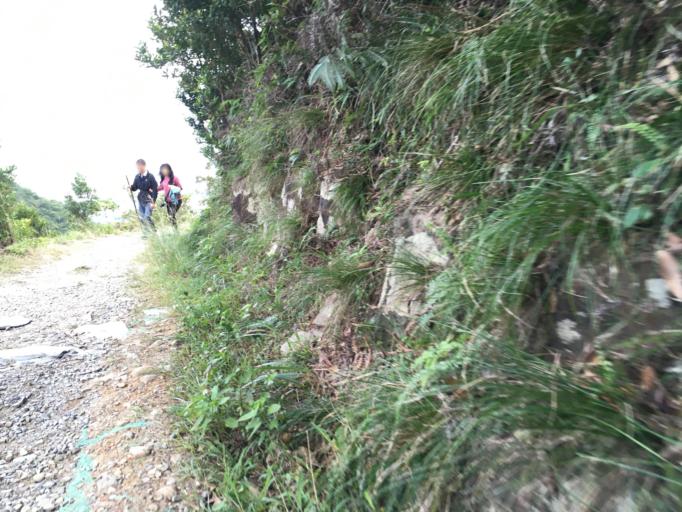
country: TW
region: Taiwan
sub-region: Yilan
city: Yilan
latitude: 24.8467
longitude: 121.7767
